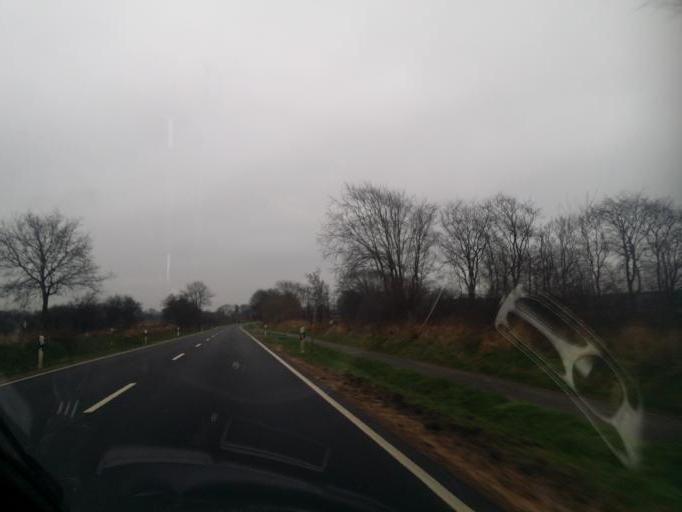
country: DE
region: Schleswig-Holstein
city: Suderheistedt
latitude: 54.2242
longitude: 9.1344
